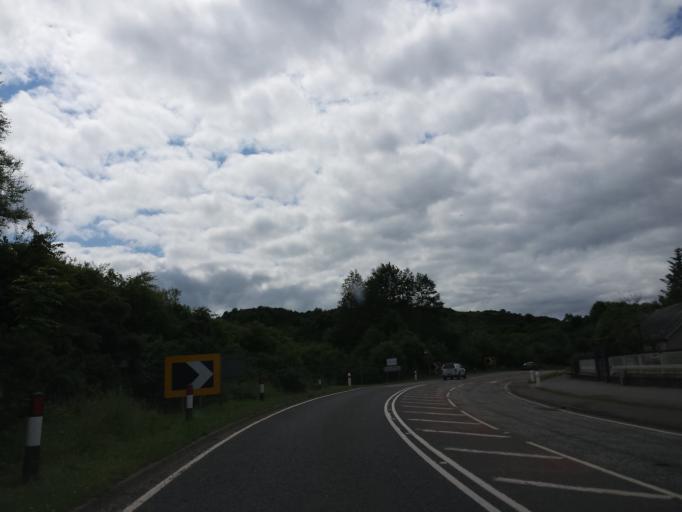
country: GB
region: Scotland
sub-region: Argyll and Bute
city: Oban
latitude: 56.4281
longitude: -5.4606
